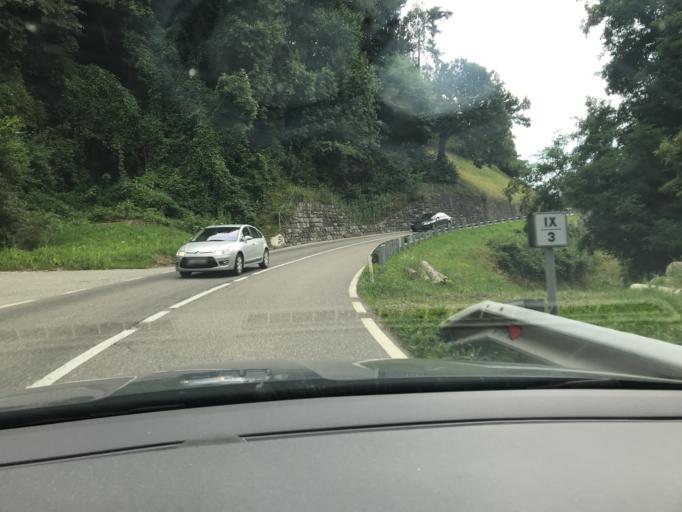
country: IT
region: Trentino-Alto Adige
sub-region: Bolzano
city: Villandro
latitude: 46.6260
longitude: 11.5536
